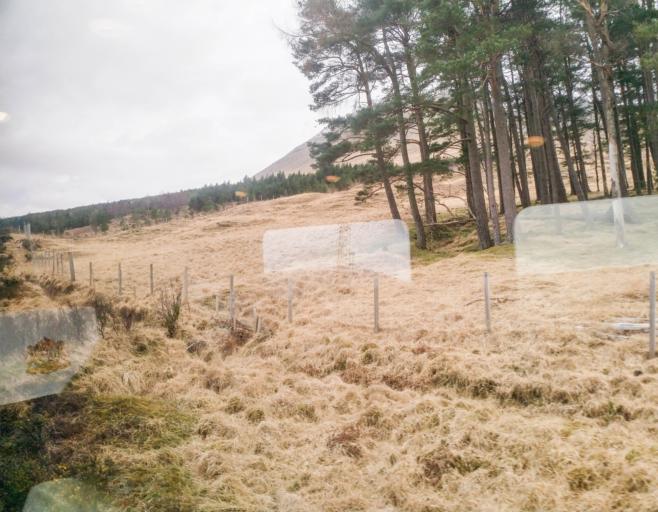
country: GB
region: Scotland
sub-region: Highland
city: Spean Bridge
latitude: 56.5187
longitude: -4.7646
